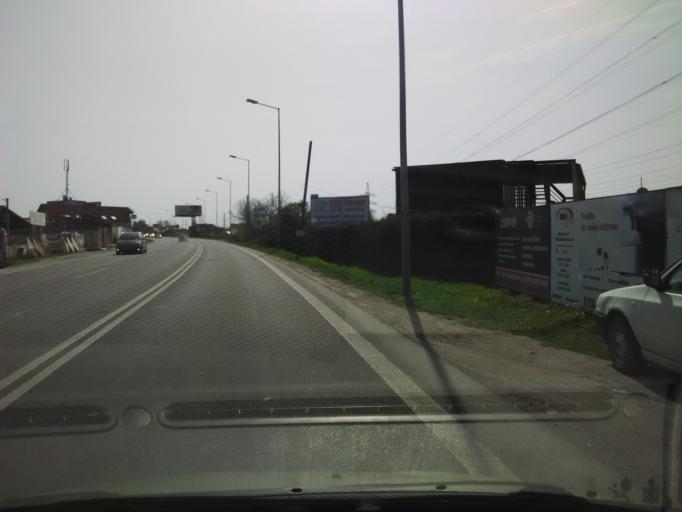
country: SK
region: Bratislavsky
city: Dunajska Luzna
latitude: 48.1268
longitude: 17.1960
